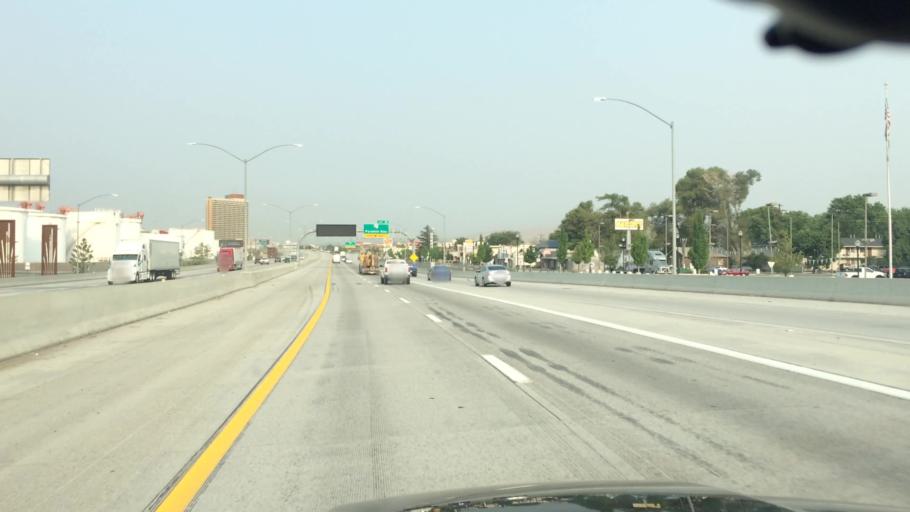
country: US
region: Nevada
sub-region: Washoe County
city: Sparks
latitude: 39.5345
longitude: -119.7428
